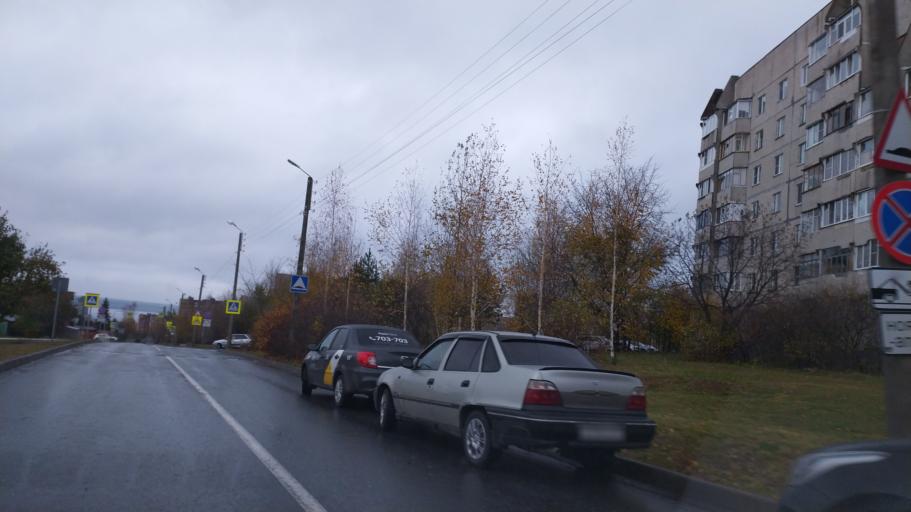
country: RU
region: Chuvashia
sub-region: Cheboksarskiy Rayon
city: Cheboksary
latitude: 56.1449
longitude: 47.1616
